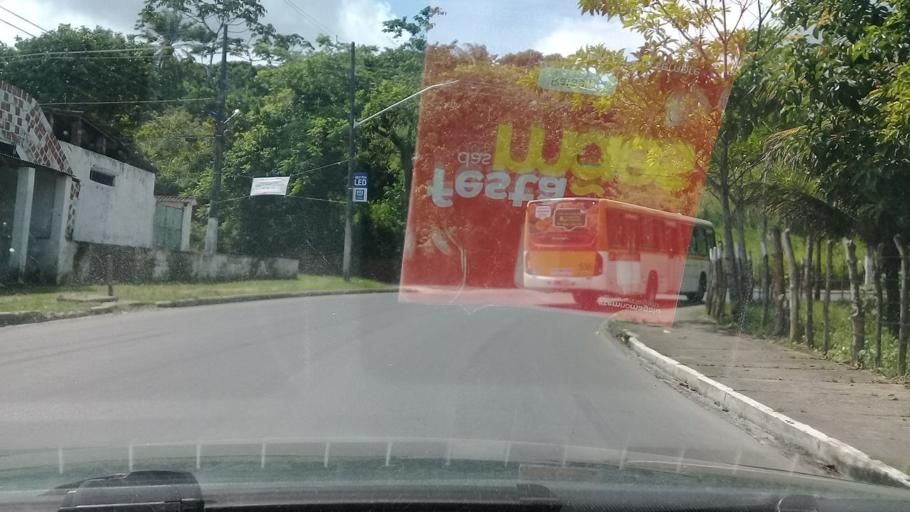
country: BR
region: Pernambuco
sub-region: Jaboatao Dos Guararapes
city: Jaboatao dos Guararapes
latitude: -8.0891
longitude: -35.0240
